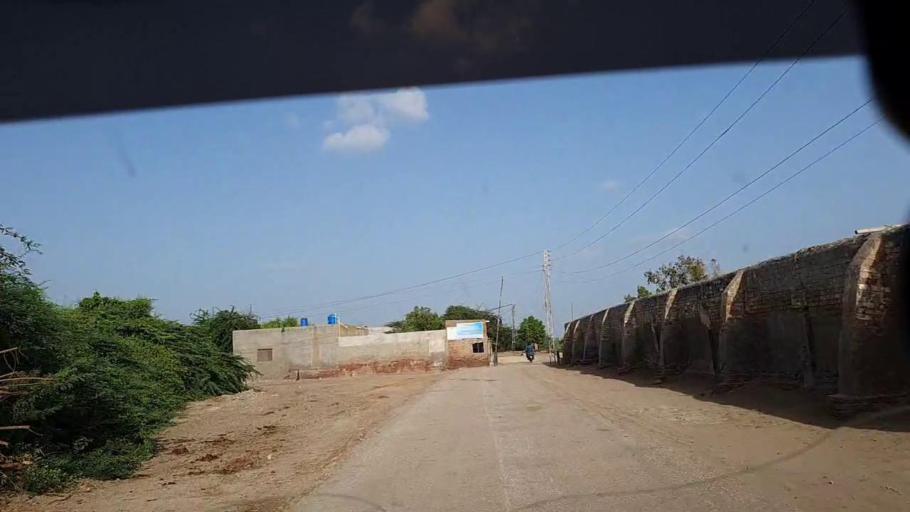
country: PK
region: Sindh
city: Badin
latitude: 24.5641
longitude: 68.9015
